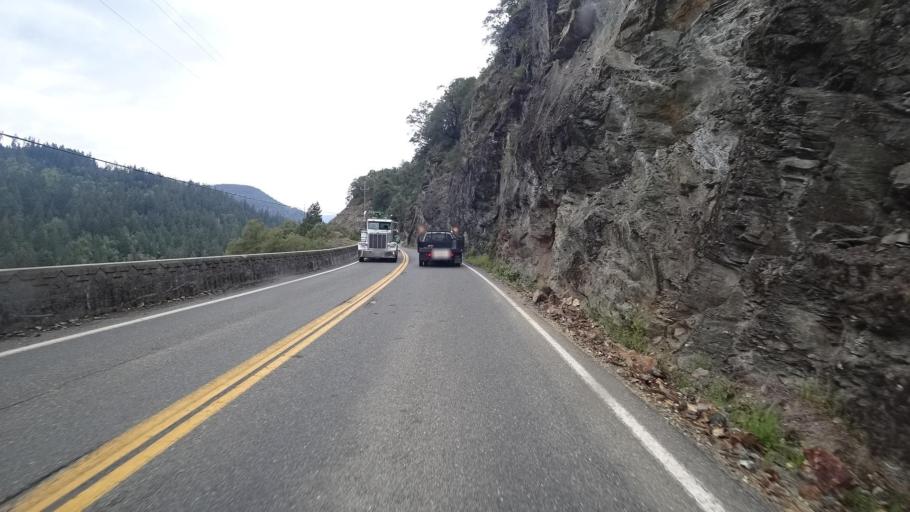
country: US
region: California
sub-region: Humboldt County
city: Willow Creek
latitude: 41.1175
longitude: -123.6883
